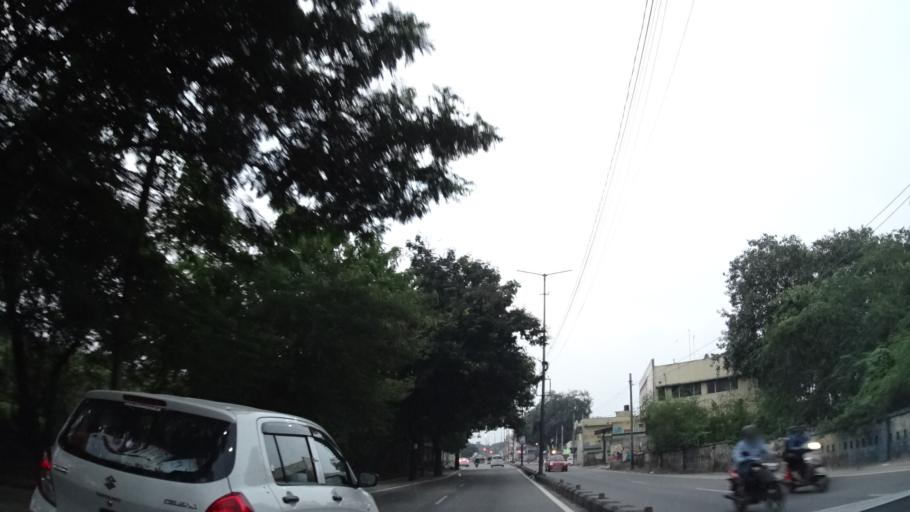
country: IN
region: Telangana
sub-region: Hyderabad
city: Malkajgiri
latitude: 17.4549
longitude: 78.4816
